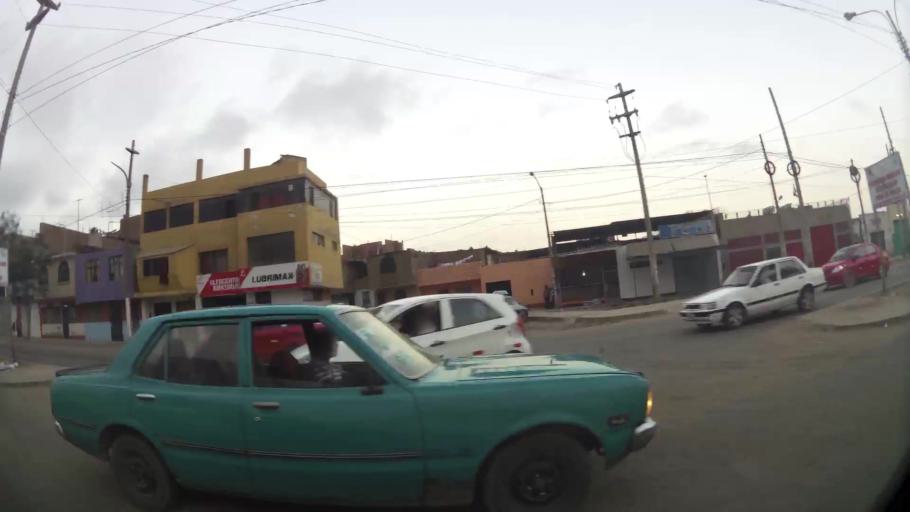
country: PE
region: La Libertad
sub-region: Provincia de Trujillo
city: El Porvenir
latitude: -8.0878
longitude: -79.0156
